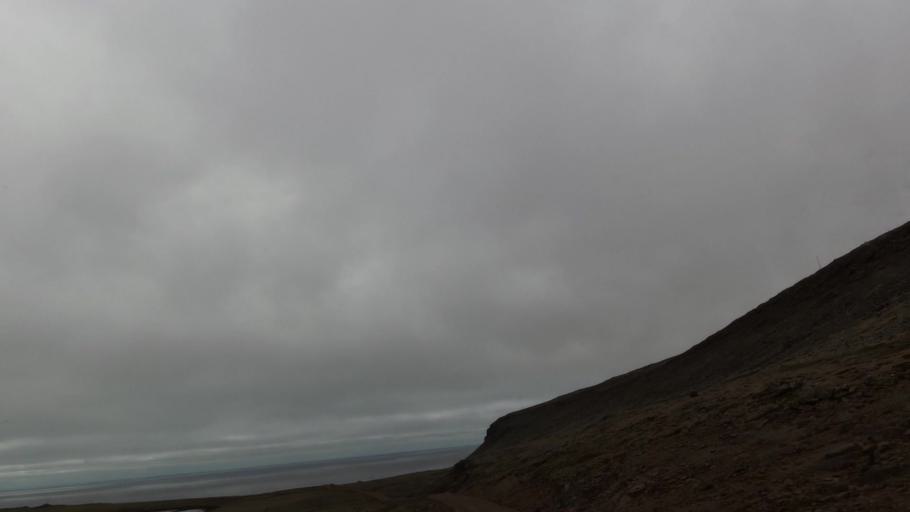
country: IS
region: West
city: Olafsvik
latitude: 65.5264
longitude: -24.4303
